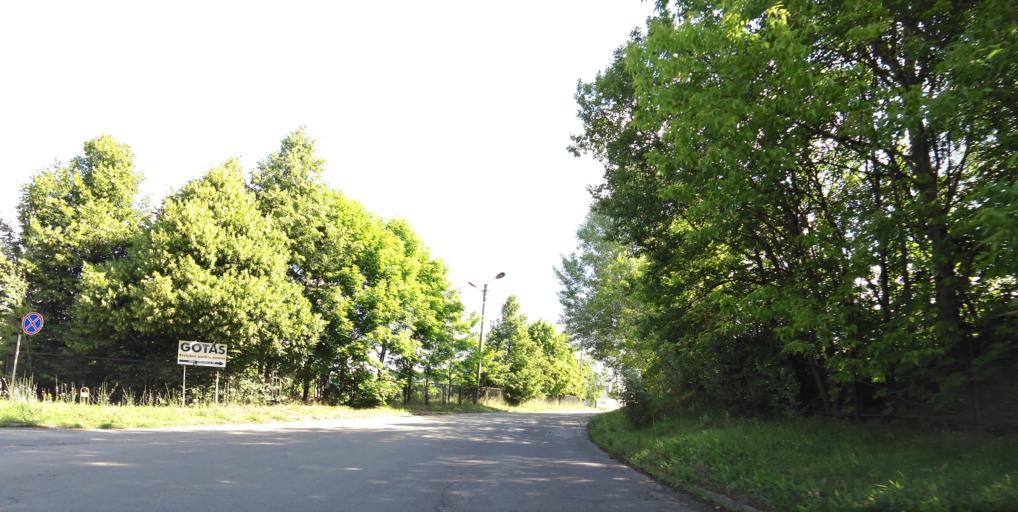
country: LT
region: Vilnius County
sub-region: Vilnius
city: Vilnius
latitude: 54.7090
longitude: 25.2722
